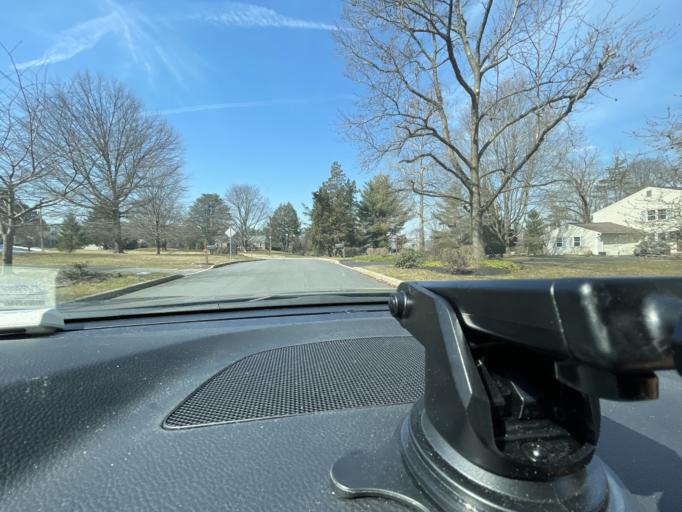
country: US
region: Pennsylvania
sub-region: Montgomery County
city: Blue Bell
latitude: 40.1591
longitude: -75.2593
